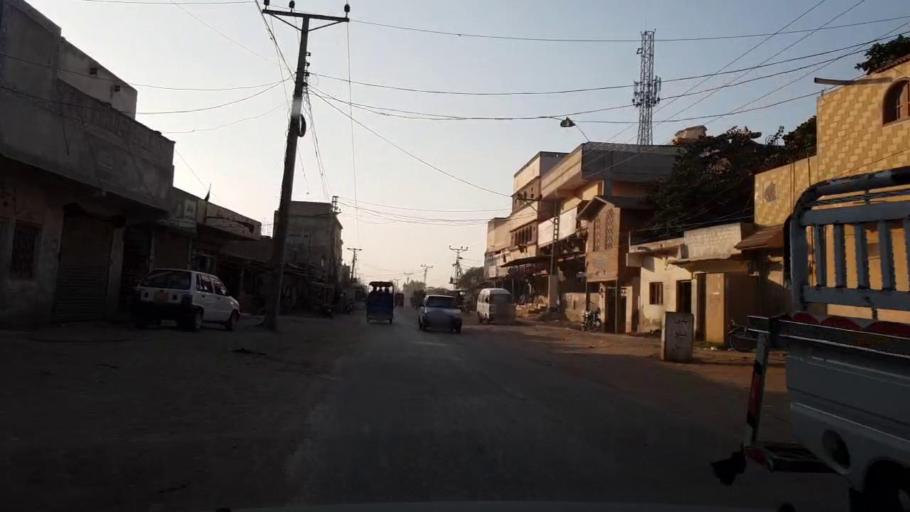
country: PK
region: Sindh
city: Thatta
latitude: 24.6069
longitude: 68.0797
